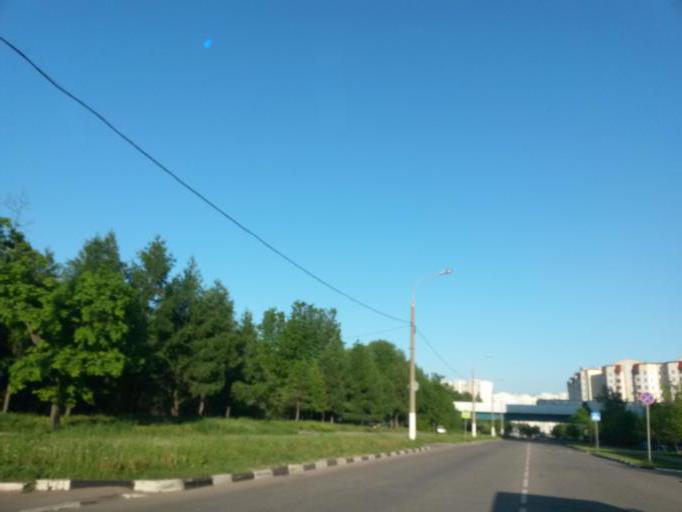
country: RU
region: Moscow
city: Annino
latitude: 55.5523
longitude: 37.5613
